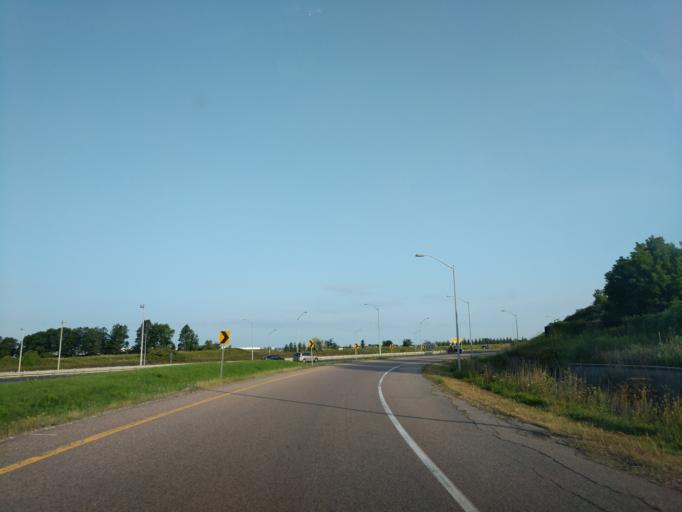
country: CA
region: Ontario
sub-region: York
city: Richmond Hill
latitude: 43.8678
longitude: -79.3749
